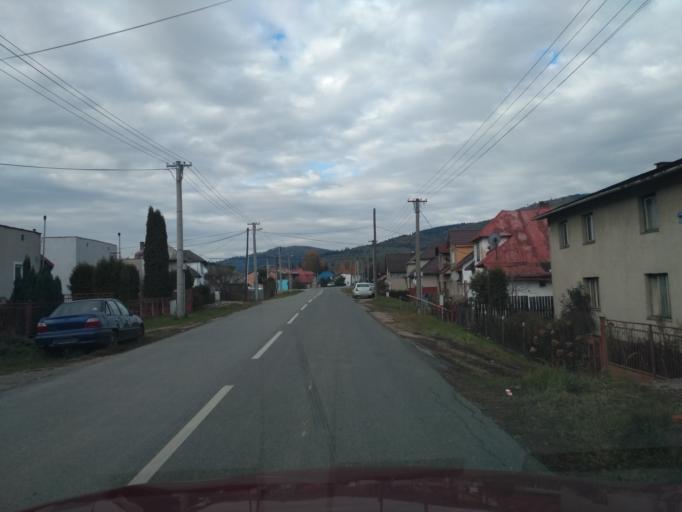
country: SK
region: Kosicky
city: Krompachy
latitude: 48.8063
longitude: 20.7261
